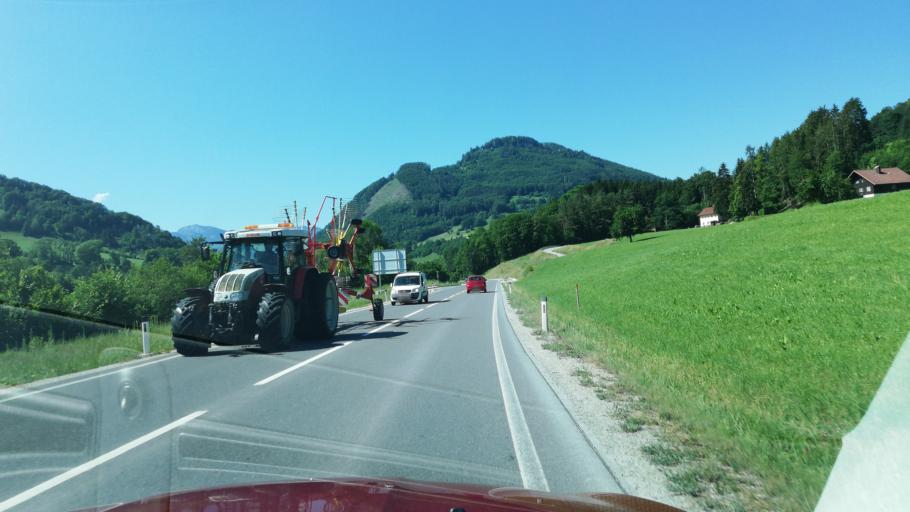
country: AT
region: Upper Austria
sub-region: Politischer Bezirk Kirchdorf an der Krems
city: Gruenburg
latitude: 47.9451
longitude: 14.2538
